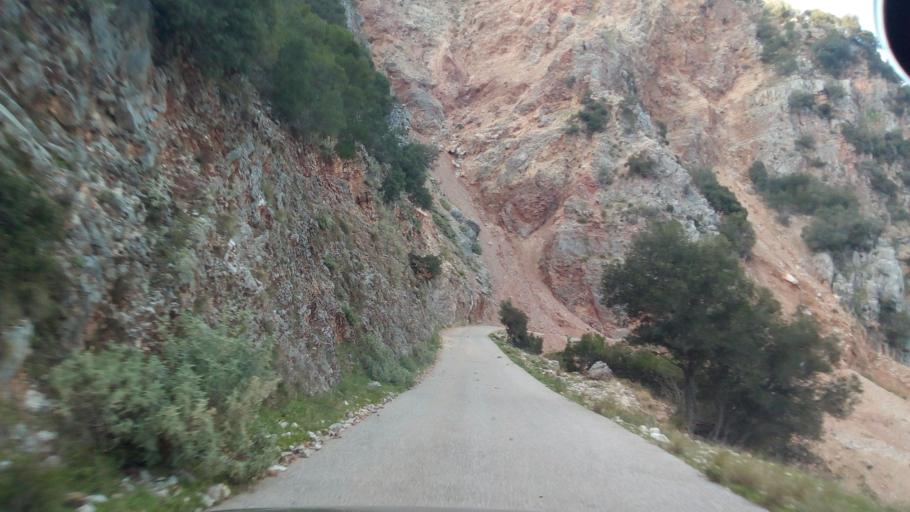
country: GR
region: West Greece
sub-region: Nomos Aitolias kai Akarnanias
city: Nafpaktos
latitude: 38.4267
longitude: 21.8199
